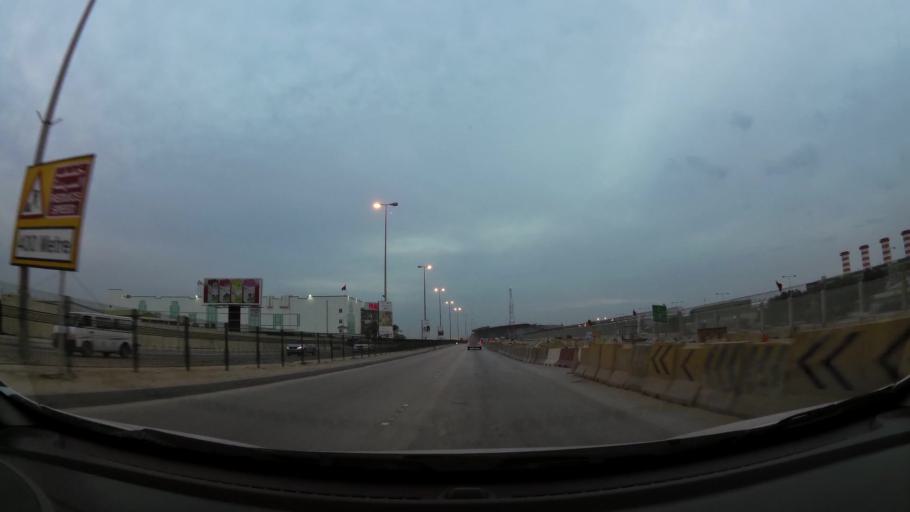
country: BH
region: Northern
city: Ar Rifa'
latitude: 26.1214
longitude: 50.5880
